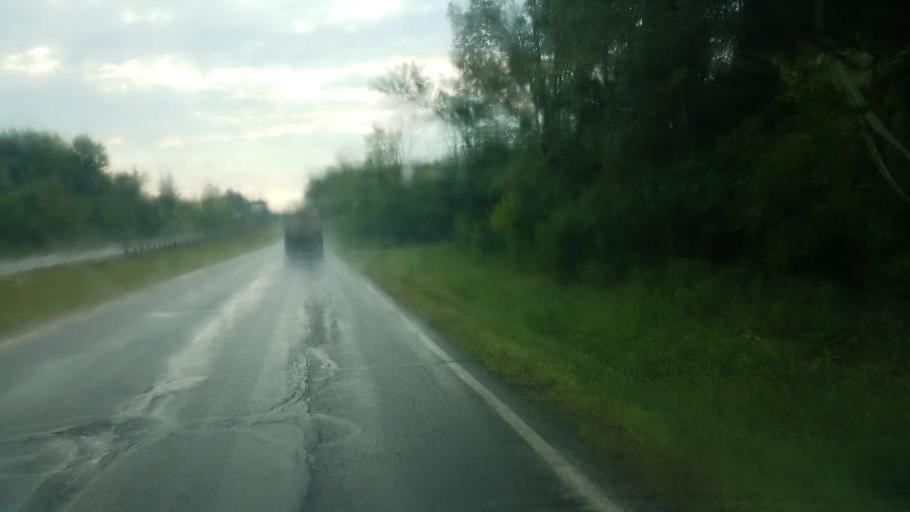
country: US
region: Ohio
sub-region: Portage County
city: Hiram
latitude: 41.3754
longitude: -81.1039
